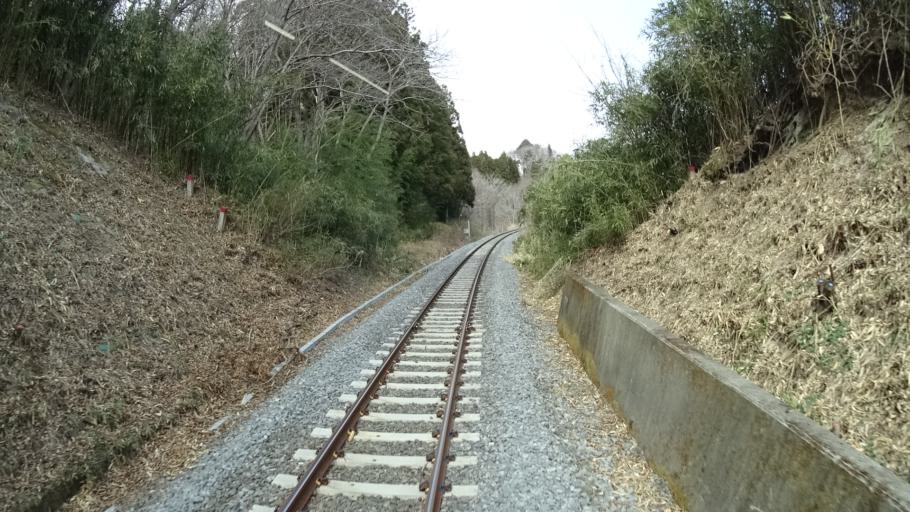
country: JP
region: Iwate
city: Miyako
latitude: 39.5919
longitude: 141.9435
